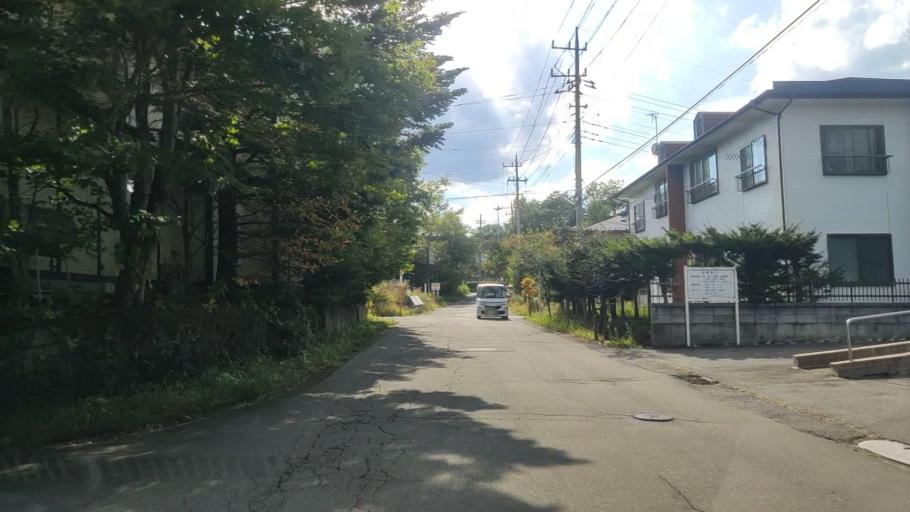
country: JP
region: Gunma
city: Nakanojomachi
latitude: 36.6190
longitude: 138.6027
